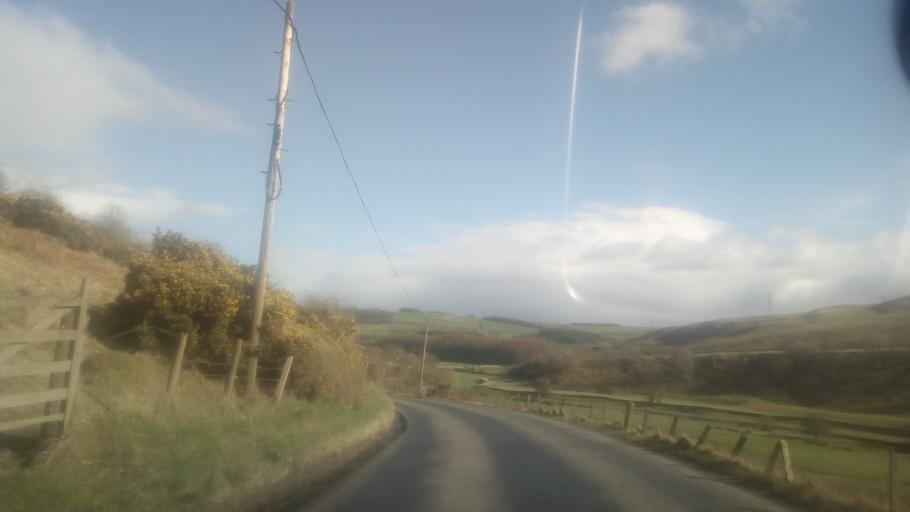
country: GB
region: Scotland
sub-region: The Scottish Borders
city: Hawick
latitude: 55.4129
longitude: -2.8482
